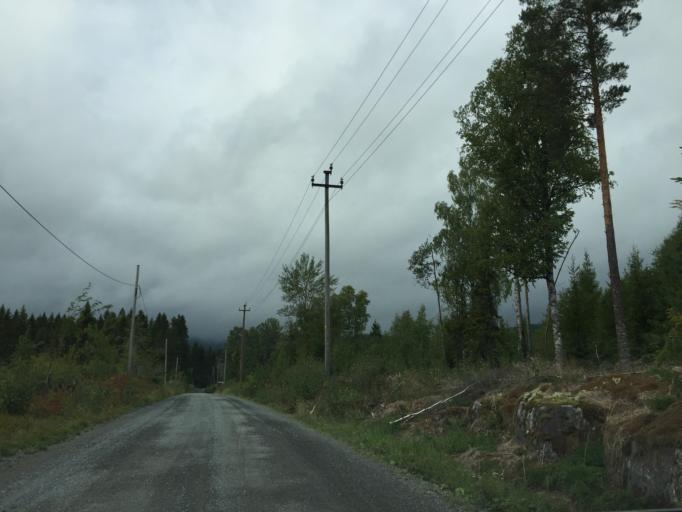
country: NO
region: Akershus
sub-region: Baerum
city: Lysaker
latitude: 60.0194
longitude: 10.5689
